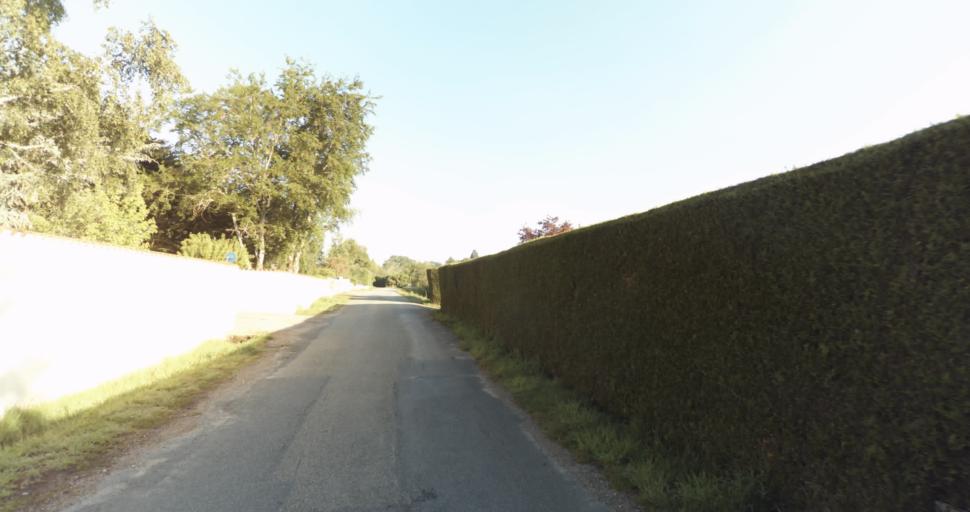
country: FR
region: Limousin
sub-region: Departement de la Haute-Vienne
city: Condat-sur-Vienne
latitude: 45.7804
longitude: 1.2937
